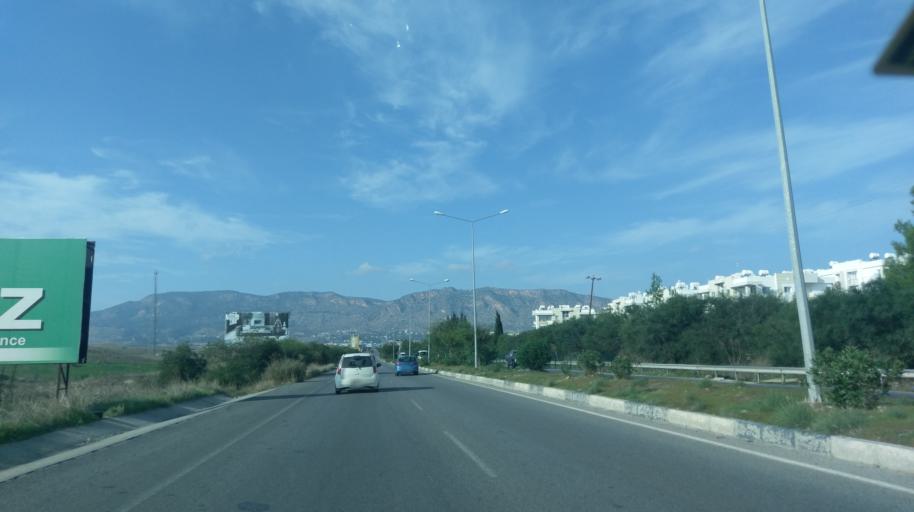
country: CY
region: Keryneia
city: Kyrenia
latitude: 35.2540
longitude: 33.3012
